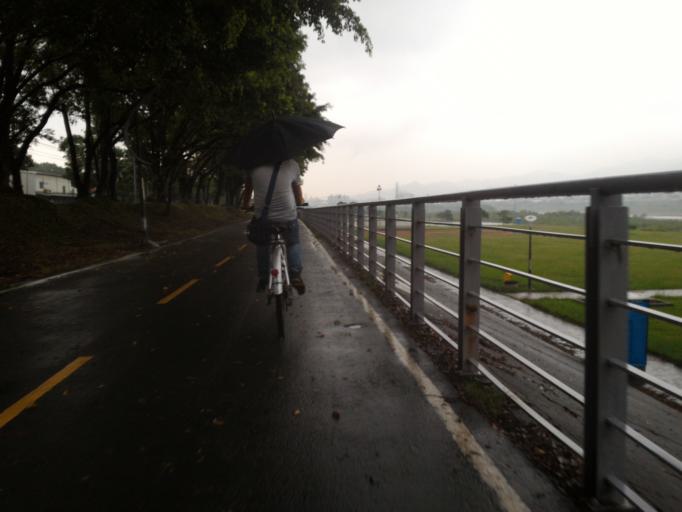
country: TW
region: Taipei
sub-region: Taipei
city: Banqiao
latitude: 24.9697
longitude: 121.4095
